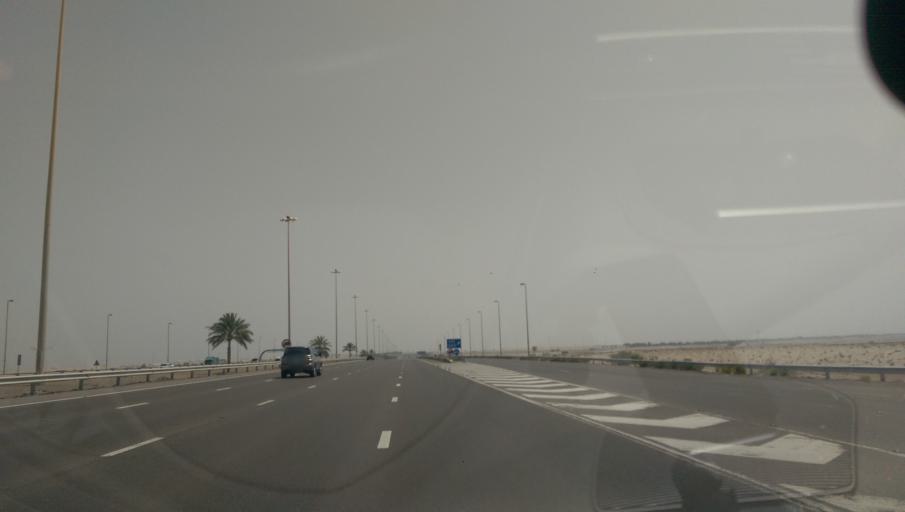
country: AE
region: Abu Dhabi
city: Abu Dhabi
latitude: 24.3962
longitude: 54.6669
